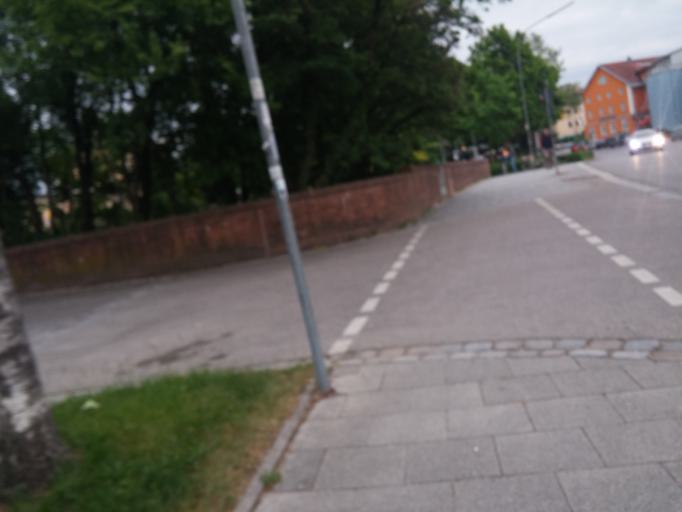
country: DE
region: Bavaria
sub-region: Upper Bavaria
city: Dachau
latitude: 48.2553
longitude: 11.4430
